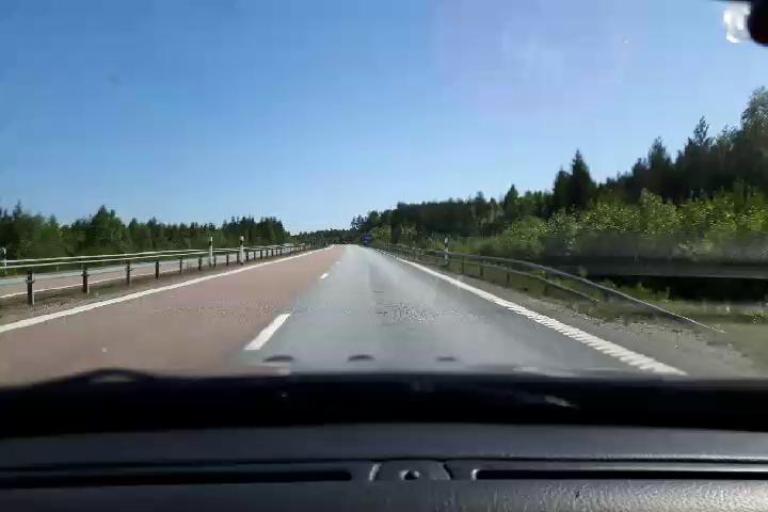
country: SE
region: Gaevleborg
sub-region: Soderhamns Kommun
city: Soderhamn
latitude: 61.4223
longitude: 16.9849
